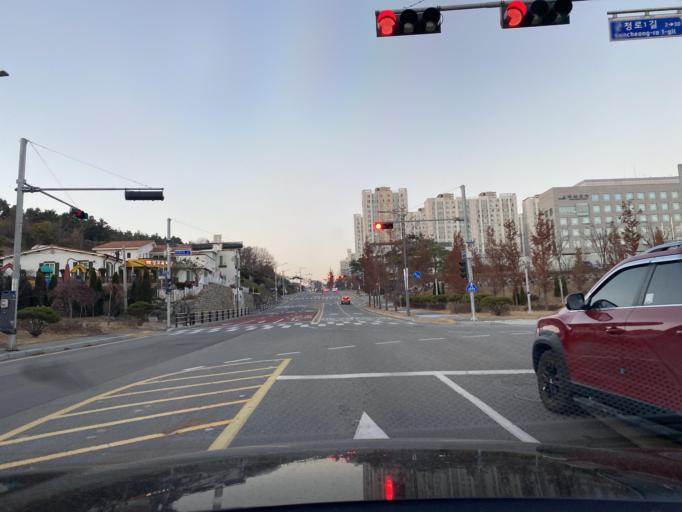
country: KR
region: Chungcheongnam-do
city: Yesan
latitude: 36.6792
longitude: 126.8435
